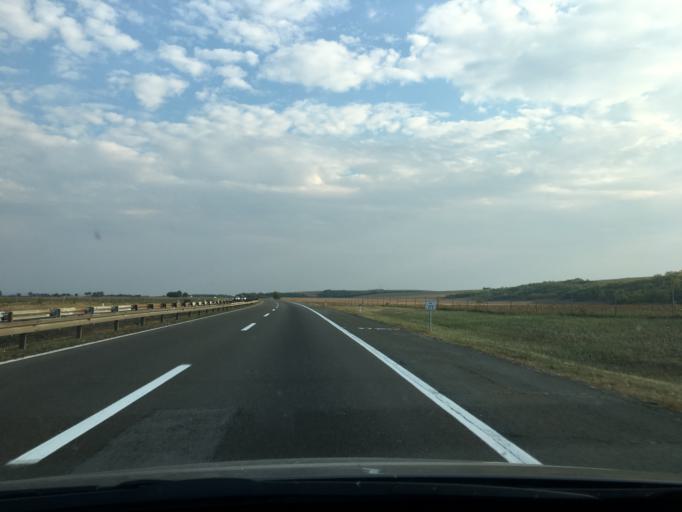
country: RS
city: Lugavcina
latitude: 44.5144
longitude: 21.0133
